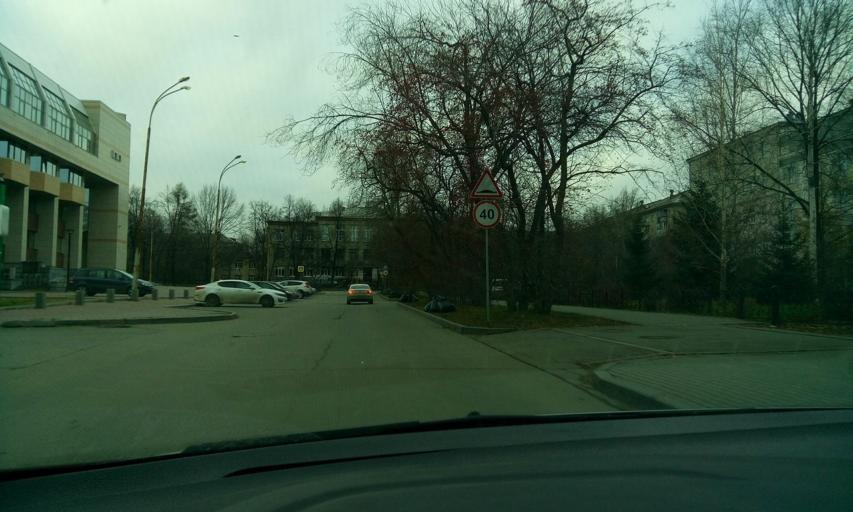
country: RU
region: Sverdlovsk
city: Yekaterinburg
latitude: 56.8502
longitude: 60.6532
